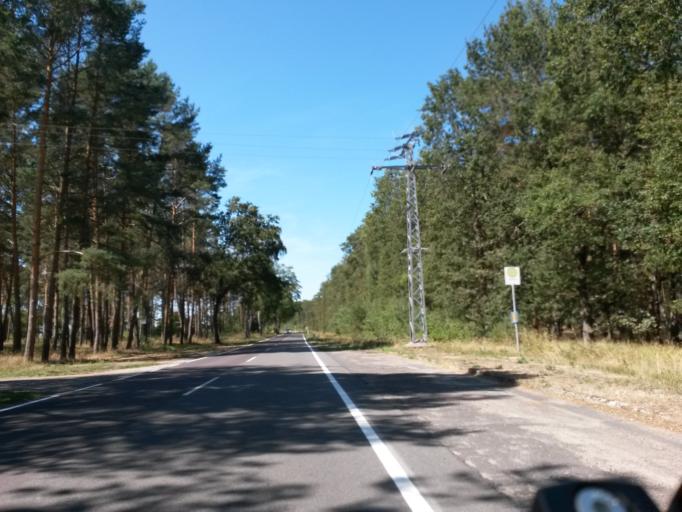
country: DE
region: Saxony-Anhalt
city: Hassel
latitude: 52.6405
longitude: 11.9526
